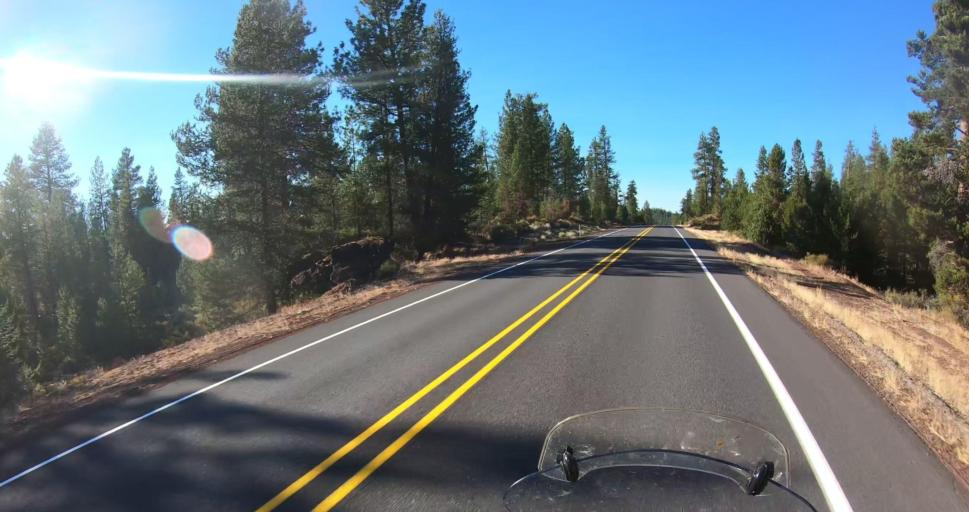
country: US
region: Oregon
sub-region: Deschutes County
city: La Pine
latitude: 43.4582
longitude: -121.3799
